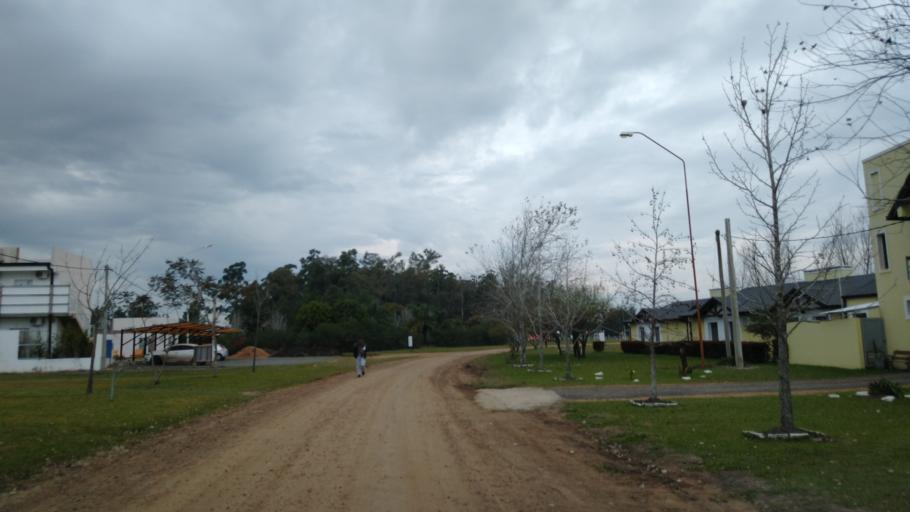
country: AR
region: Entre Rios
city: Chajari
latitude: -30.7432
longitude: -58.0099
